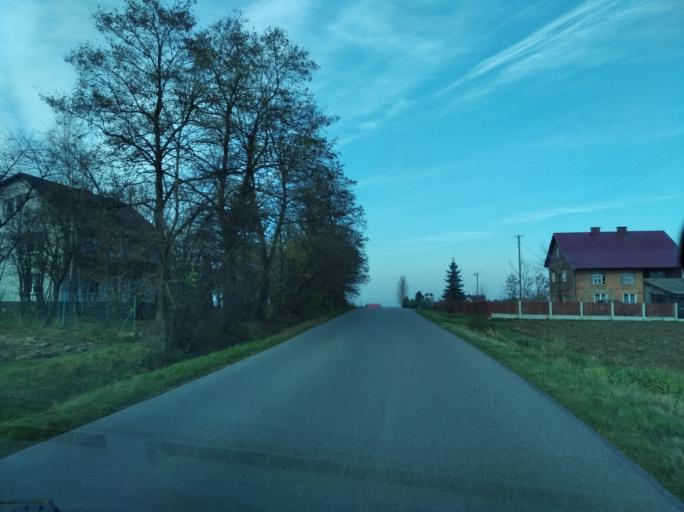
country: PL
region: Subcarpathian Voivodeship
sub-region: Powiat ropczycko-sedziszowski
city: Zagorzyce
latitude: 49.9793
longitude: 21.7142
